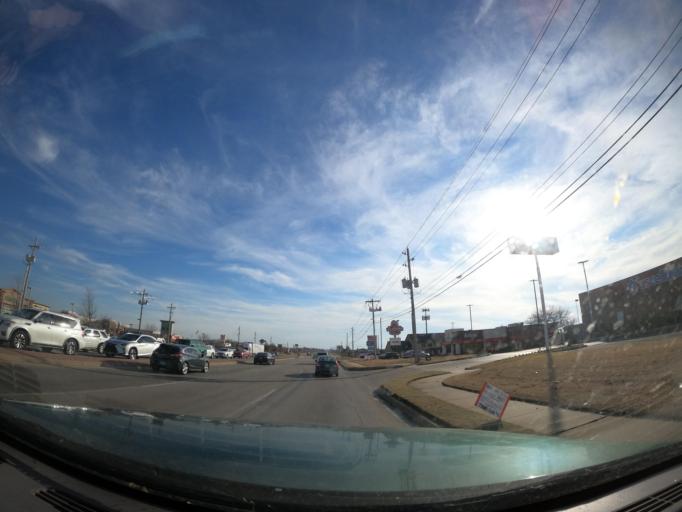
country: US
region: Oklahoma
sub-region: Tulsa County
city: Bixby
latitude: 36.0168
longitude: -95.8866
